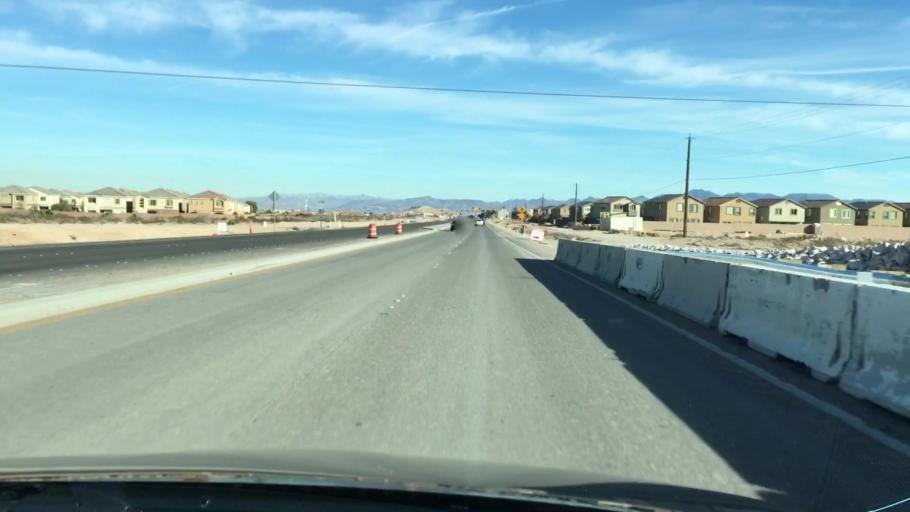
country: US
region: Nevada
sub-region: Clark County
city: Enterprise
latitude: 36.0215
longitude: -115.3062
